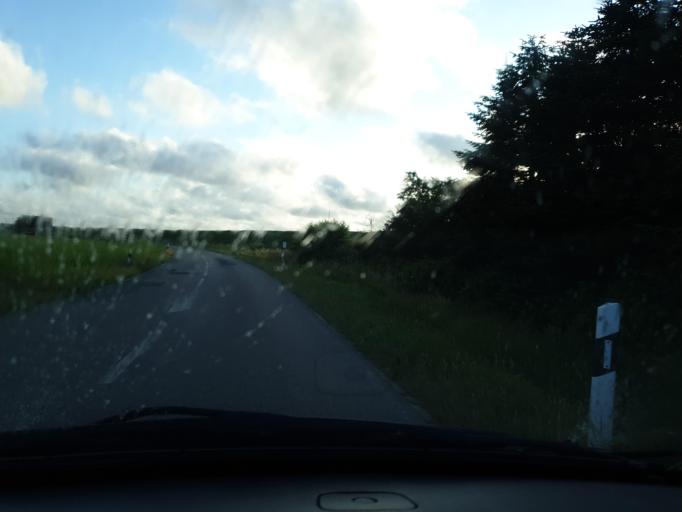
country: DE
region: Schleswig-Holstein
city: Busenwurth
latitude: 54.0585
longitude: 9.0174
